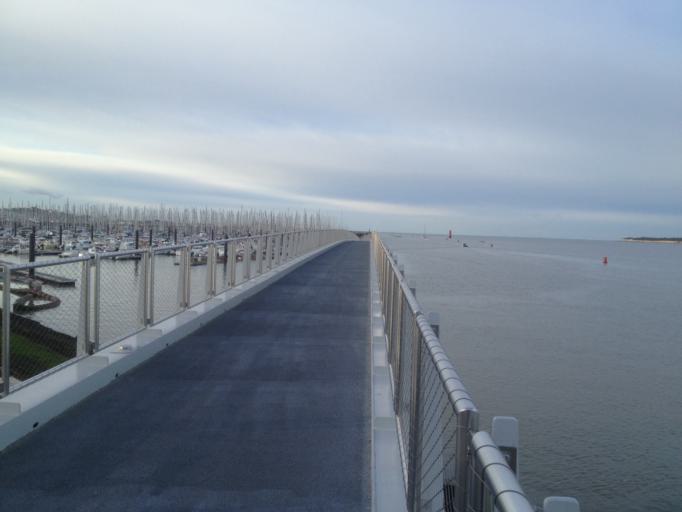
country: FR
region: Poitou-Charentes
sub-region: Departement de la Charente-Maritime
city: La Rochelle
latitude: 46.1523
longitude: -1.1597
